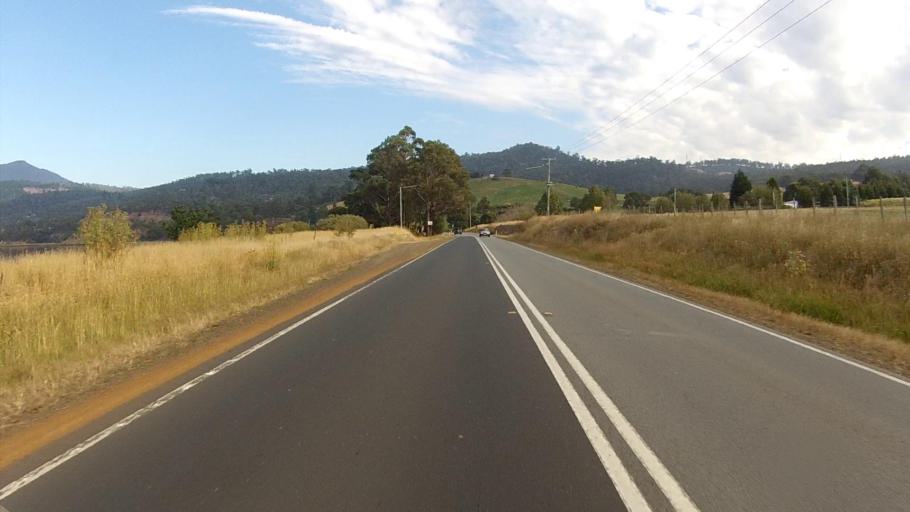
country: AU
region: Tasmania
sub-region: Brighton
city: Bridgewater
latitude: -42.7281
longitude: 147.2058
